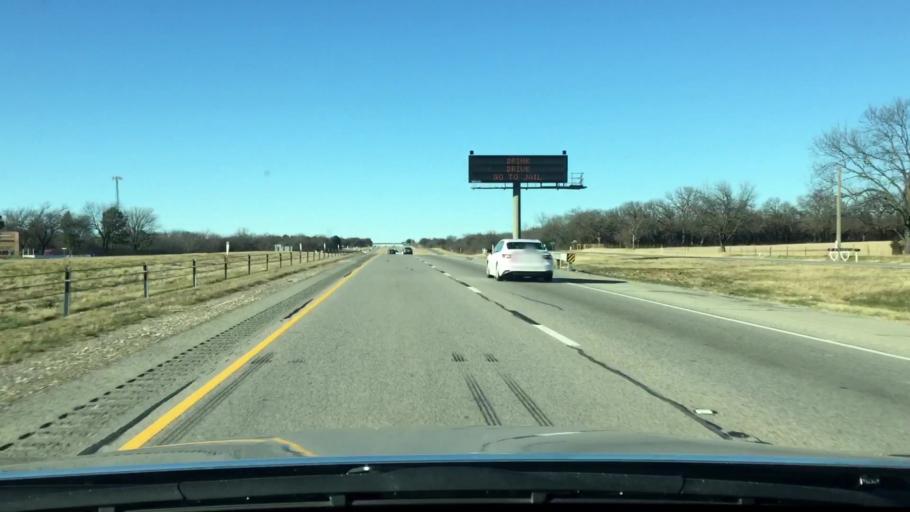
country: US
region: Texas
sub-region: Johnson County
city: Alvarado
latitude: 32.3676
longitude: -97.2013
